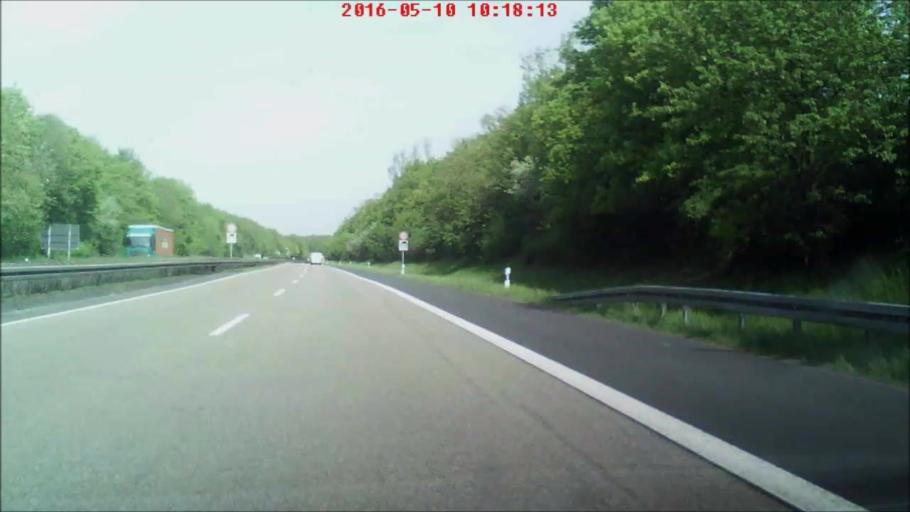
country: DE
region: Hesse
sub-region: Regierungsbezirk Kassel
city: Kunzell
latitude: 50.5265
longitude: 9.7377
